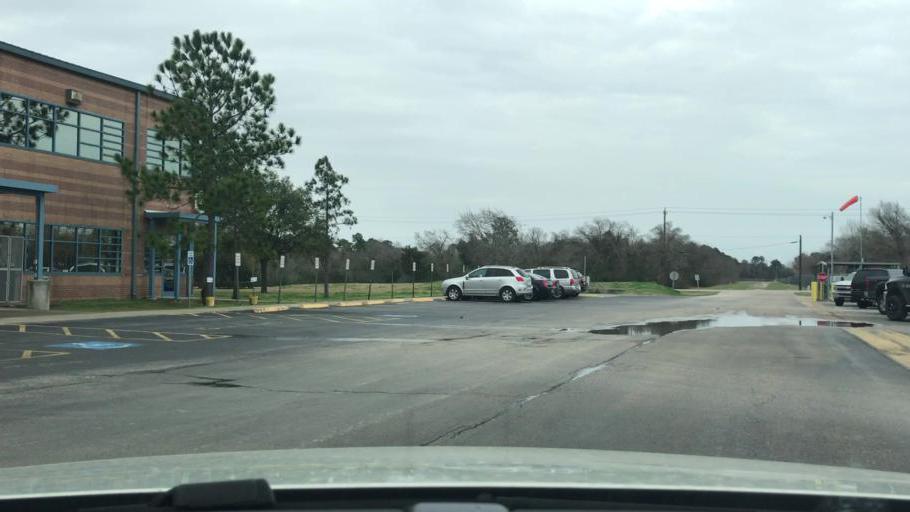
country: US
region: Texas
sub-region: Harris County
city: Baytown
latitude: 29.7647
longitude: -94.9131
